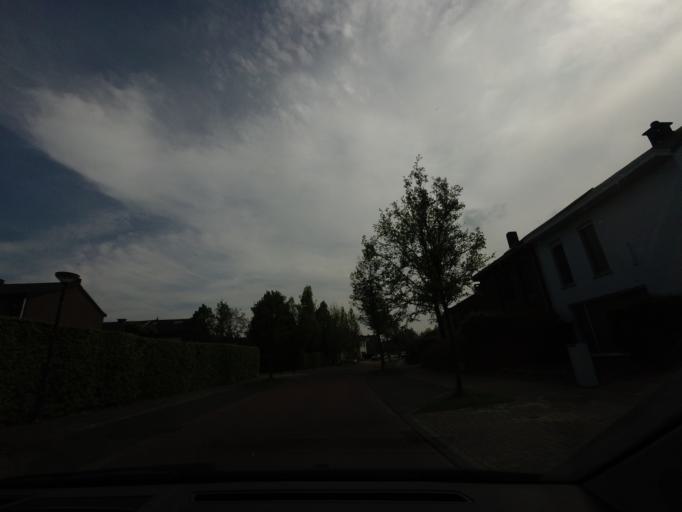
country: BE
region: Flanders
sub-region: Provincie Antwerpen
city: Kontich
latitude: 51.1138
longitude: 4.4533
